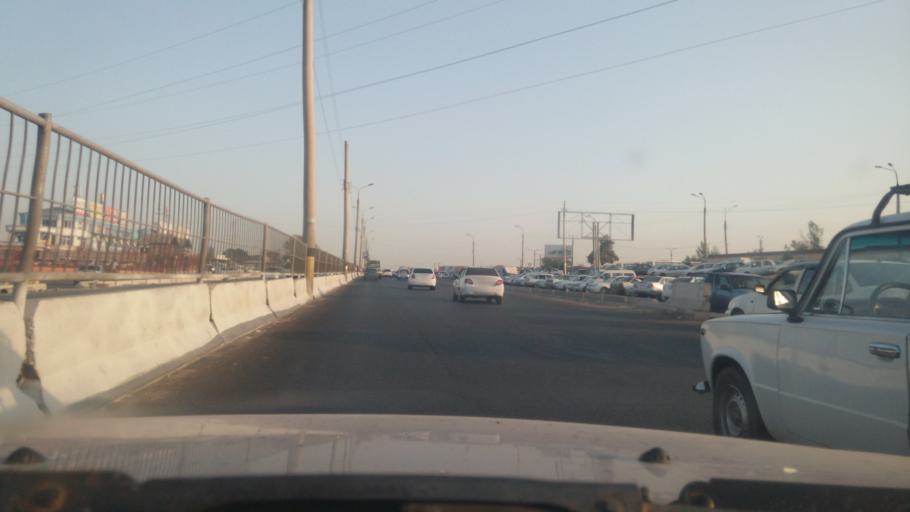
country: UZ
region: Toshkent Shahri
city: Tashkent
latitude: 41.2412
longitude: 69.1669
